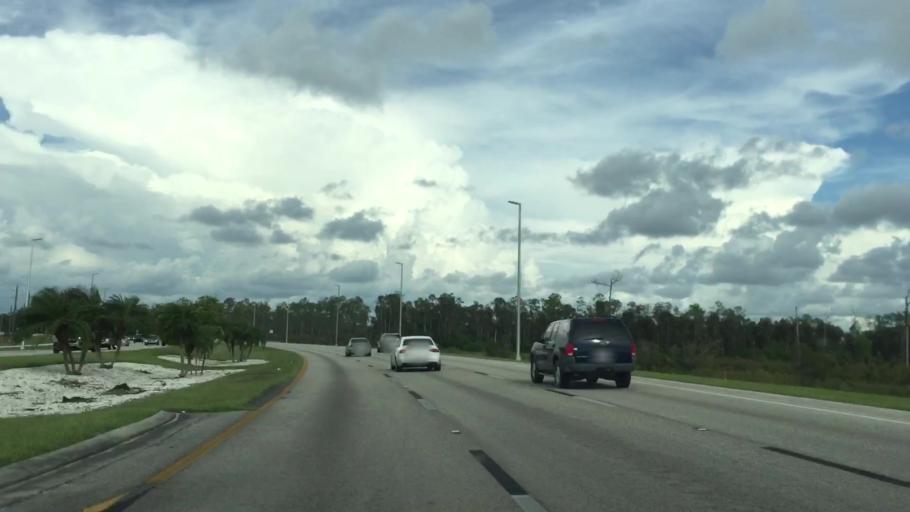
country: US
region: Florida
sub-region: Lee County
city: Gateway
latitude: 26.6147
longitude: -81.7786
